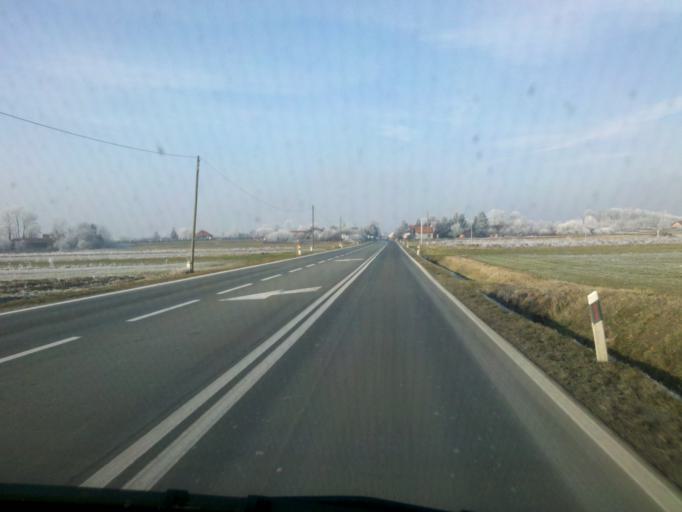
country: HR
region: Virovitick-Podravska
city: Pitomaca
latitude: 45.9762
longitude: 17.1697
